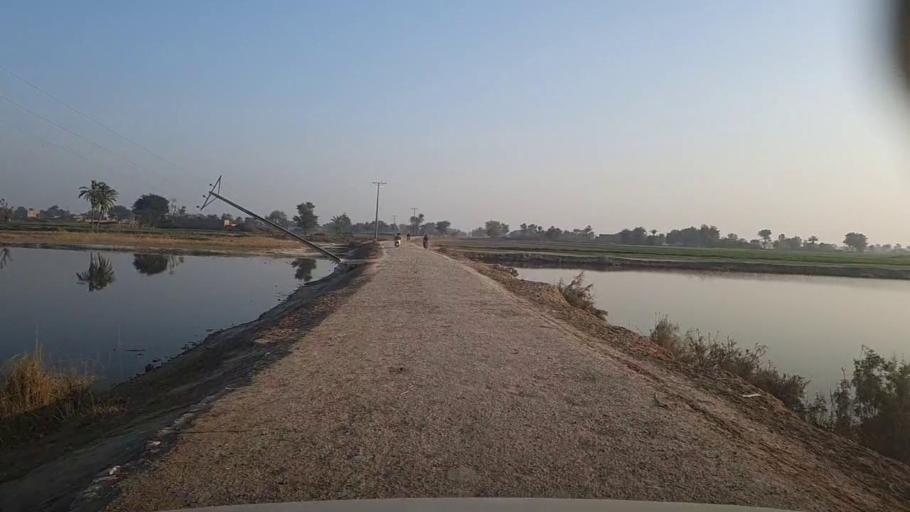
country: PK
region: Sindh
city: Khairpur
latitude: 28.0641
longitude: 69.7529
